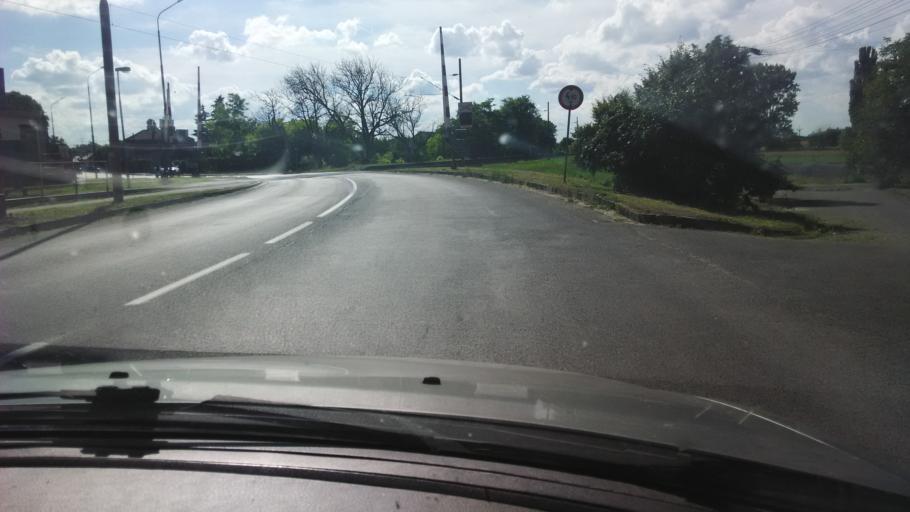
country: SK
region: Nitriansky
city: Surany
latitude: 48.0908
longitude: 18.1978
